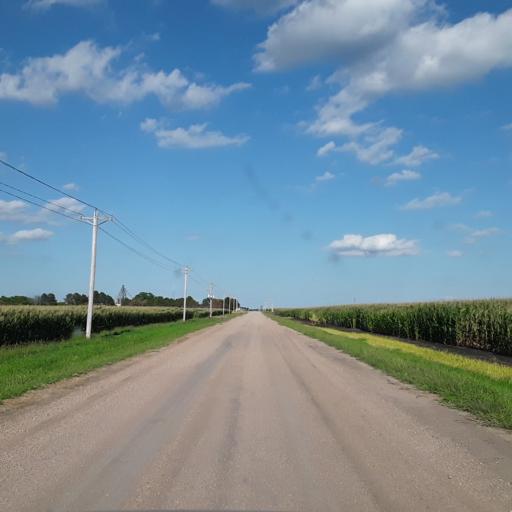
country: US
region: Nebraska
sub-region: Hall County
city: Wood River
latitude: 40.9168
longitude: -98.5943
